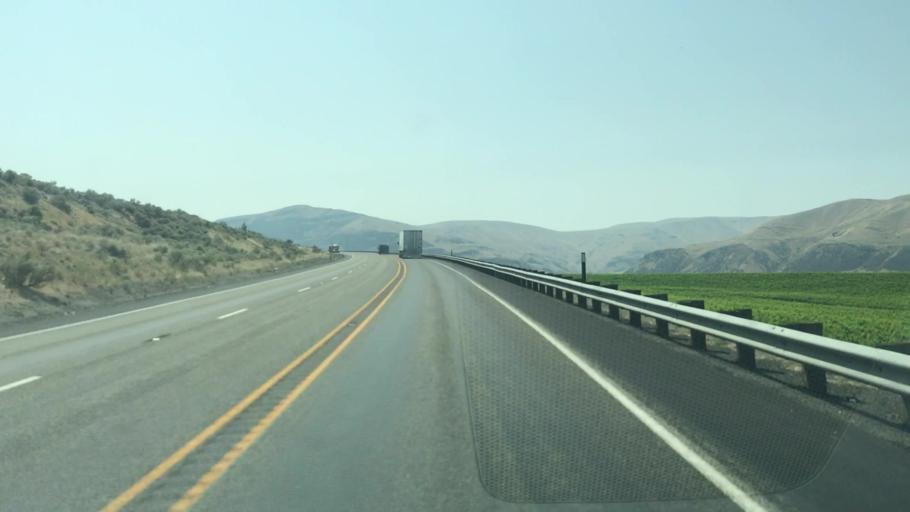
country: US
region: Washington
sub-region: Grant County
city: Quincy
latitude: 47.2563
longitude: -120.0768
